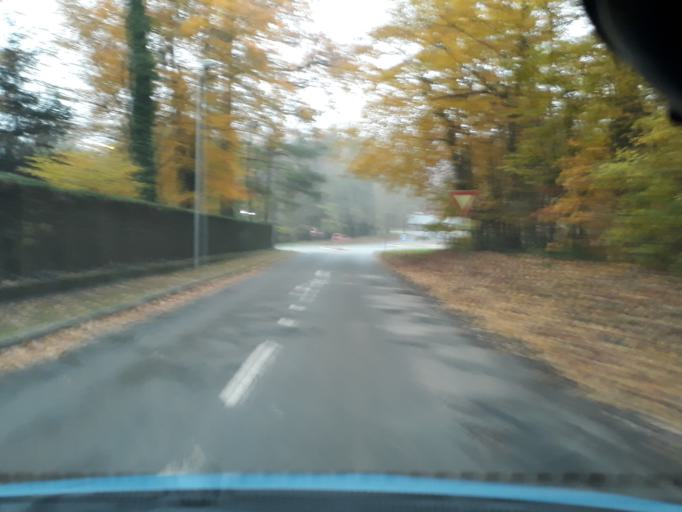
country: FR
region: Ile-de-France
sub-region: Departement de Seine-et-Marne
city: Veneux-les-Sablons
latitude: 48.3788
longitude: 2.7822
